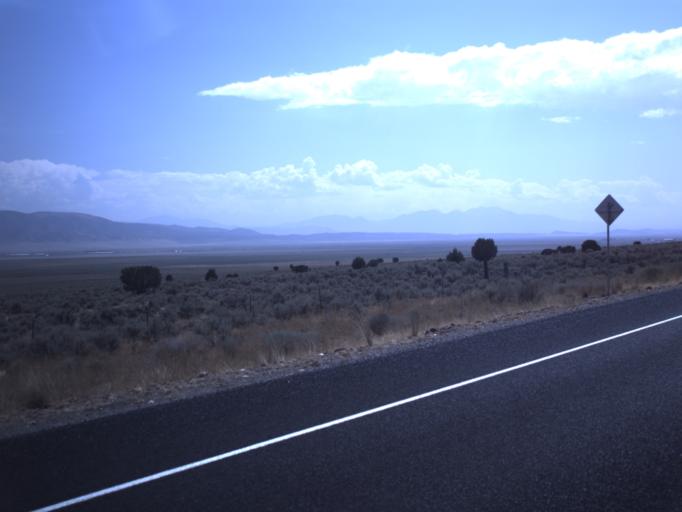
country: US
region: Utah
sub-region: Utah County
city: Eagle Mountain
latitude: 40.3187
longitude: -112.1025
